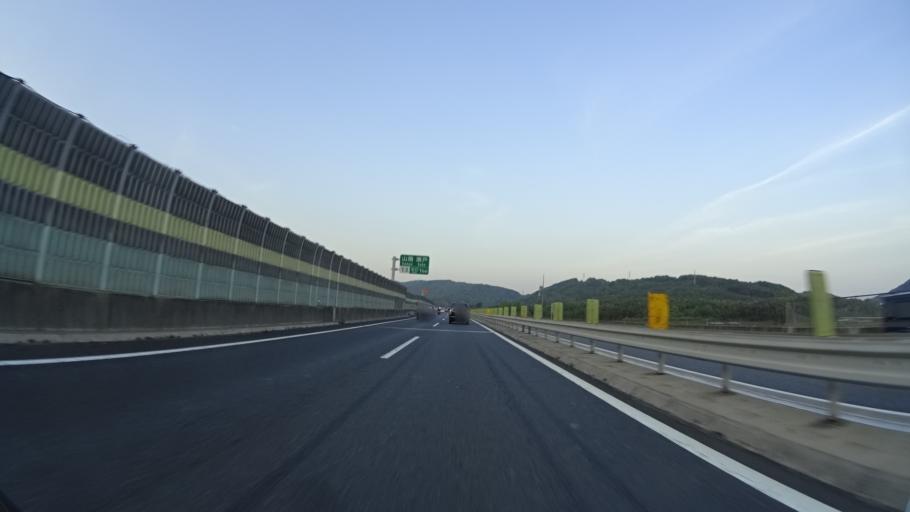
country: JP
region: Okayama
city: Okayama-shi
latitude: 34.7383
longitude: 134.0115
